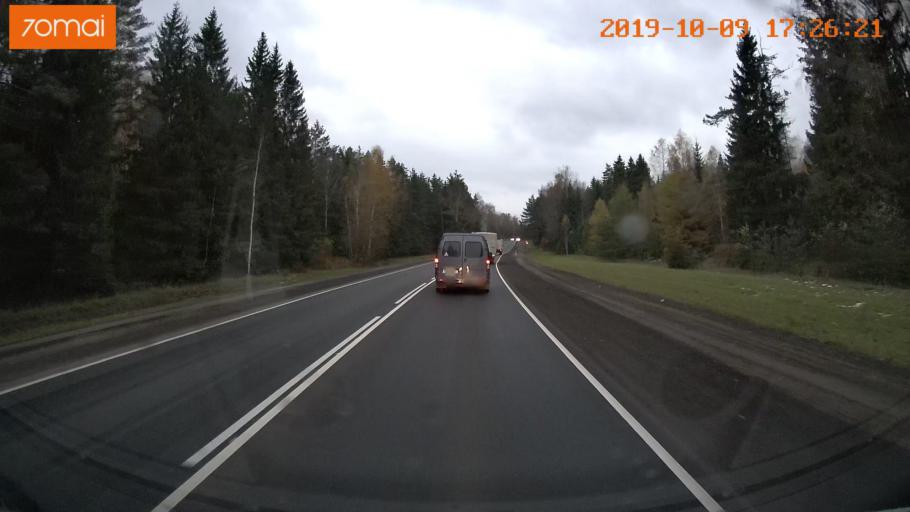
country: RU
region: Ivanovo
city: Furmanov
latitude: 57.1743
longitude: 41.0809
